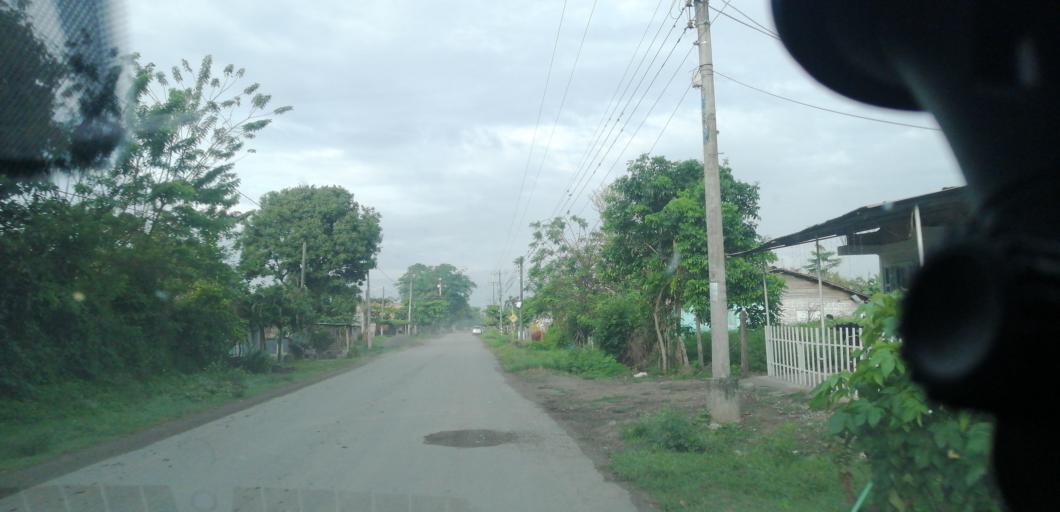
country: CO
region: Valle del Cauca
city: Palmira
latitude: 3.5369
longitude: -76.3510
